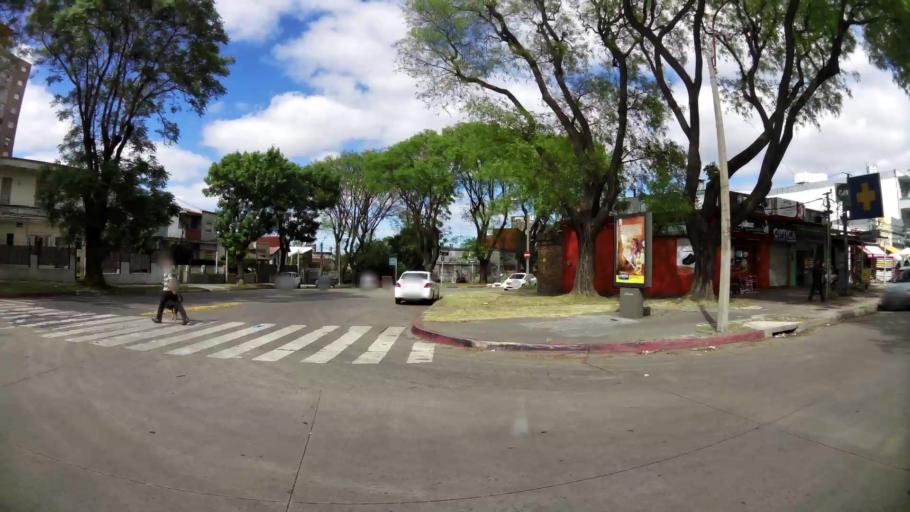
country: UY
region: Montevideo
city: Montevideo
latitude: -34.8878
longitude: -56.1289
